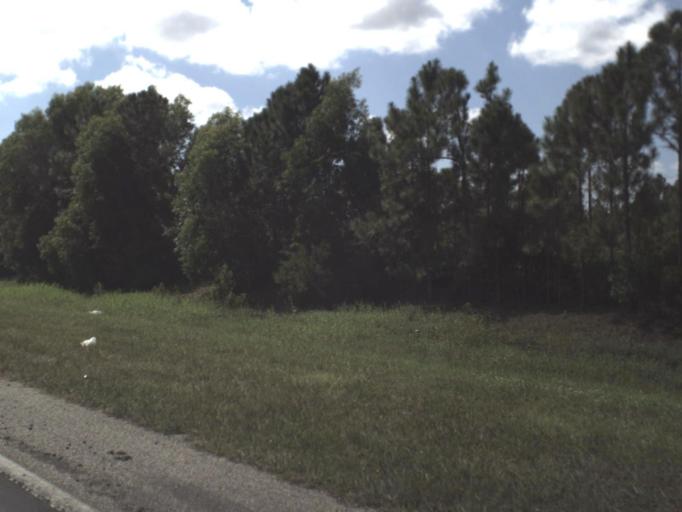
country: US
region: Florida
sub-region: Lee County
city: Suncoast Estates
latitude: 26.7586
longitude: -81.9251
